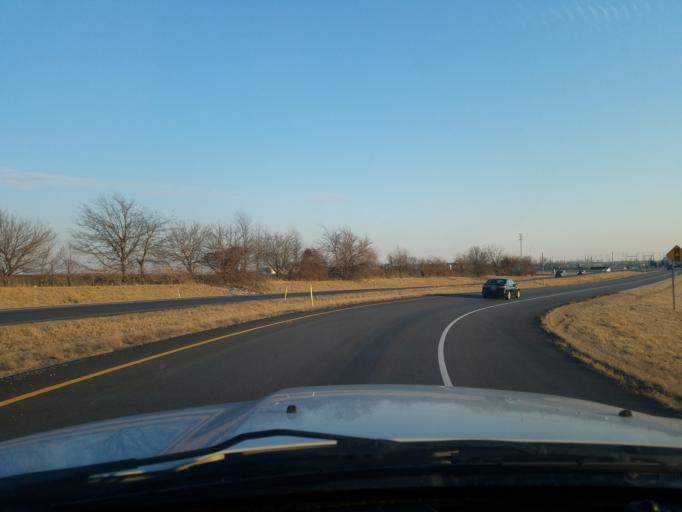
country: US
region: Indiana
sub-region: Vanderburgh County
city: Melody Hill
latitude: 37.9995
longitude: -87.4648
